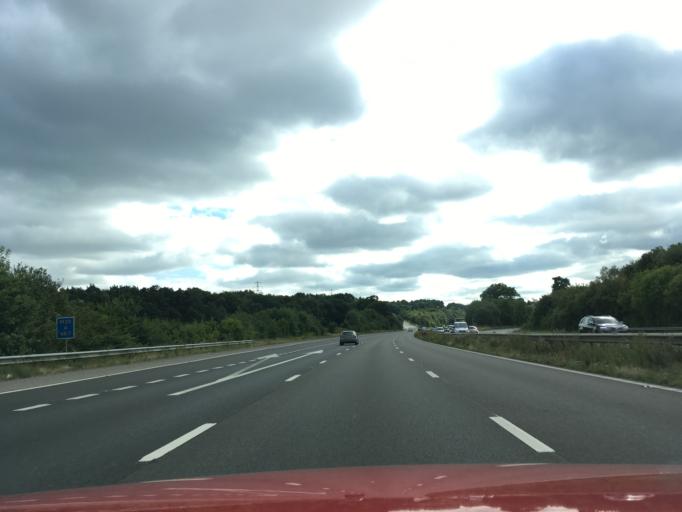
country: GB
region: England
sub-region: West Sussex
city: Maidenbower
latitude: 51.1083
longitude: -0.1399
